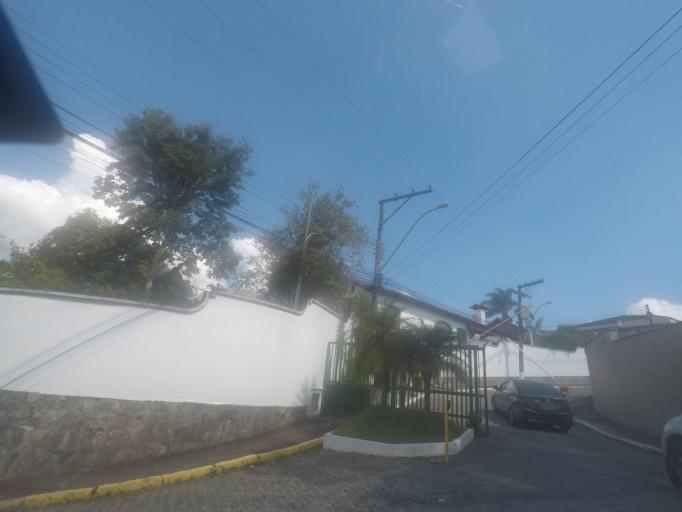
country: BR
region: Rio de Janeiro
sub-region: Petropolis
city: Petropolis
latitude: -22.5083
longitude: -43.1787
